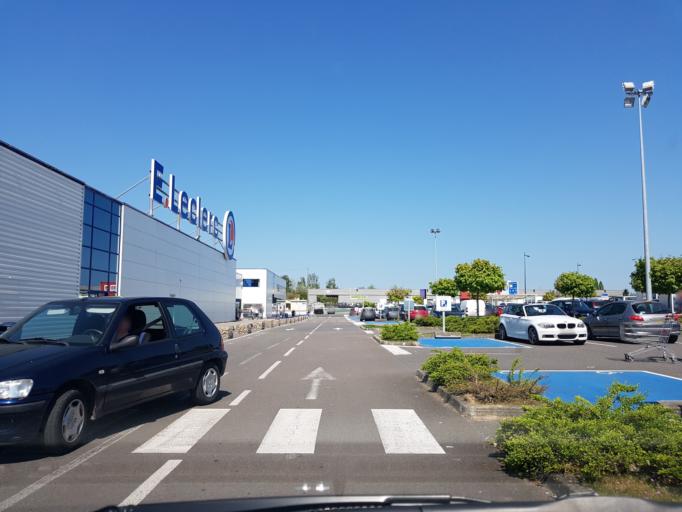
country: FR
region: Limousin
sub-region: Departement de la Haute-Vienne
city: Saint-Junien
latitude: 45.8954
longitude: 0.9156
